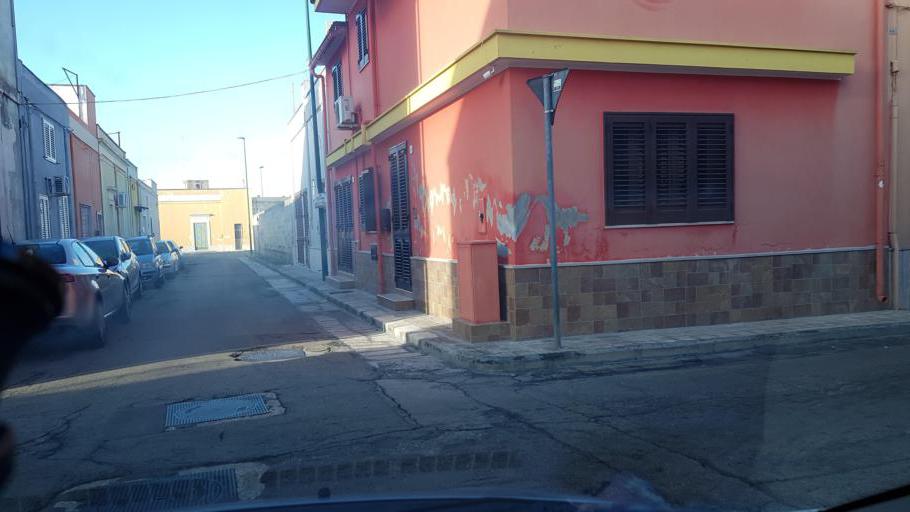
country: IT
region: Apulia
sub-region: Provincia di Lecce
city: Guagnano
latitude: 40.3994
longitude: 17.9512
